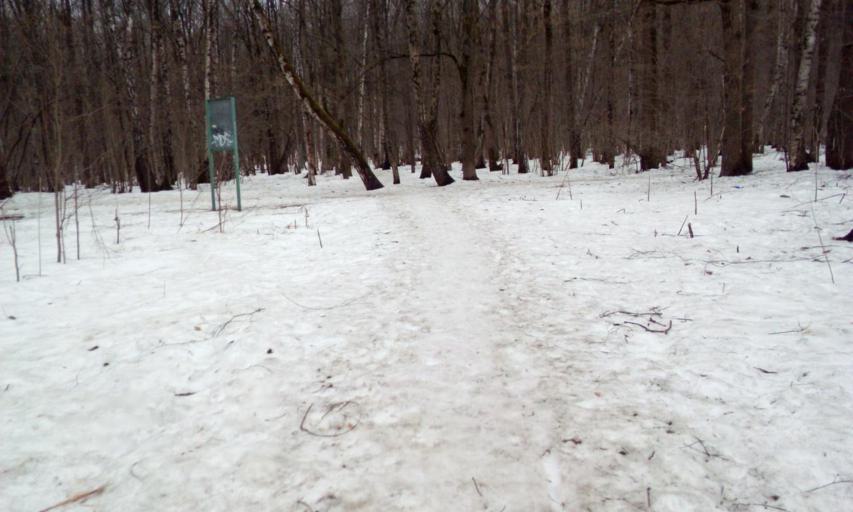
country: RU
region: Moscow
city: Troparevo
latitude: 55.6381
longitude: 37.4843
